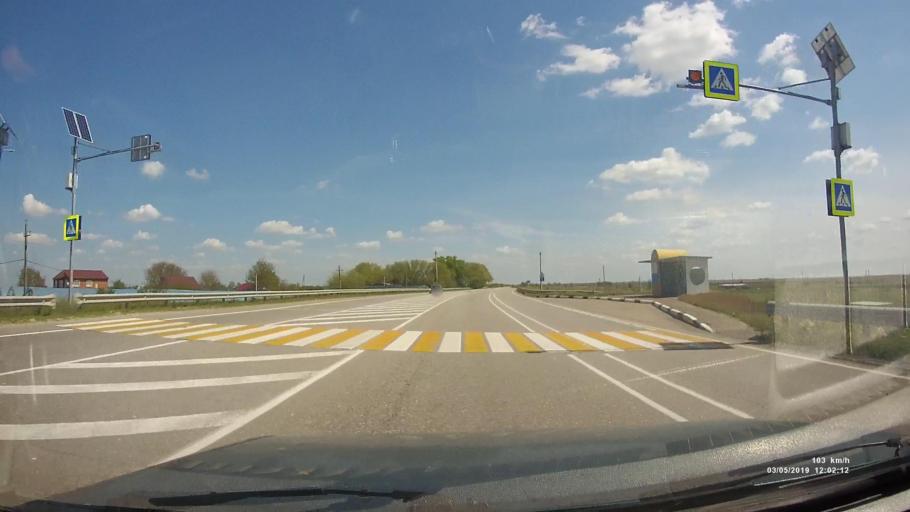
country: RU
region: Rostov
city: Bagayevskaya
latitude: 47.2715
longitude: 40.3615
